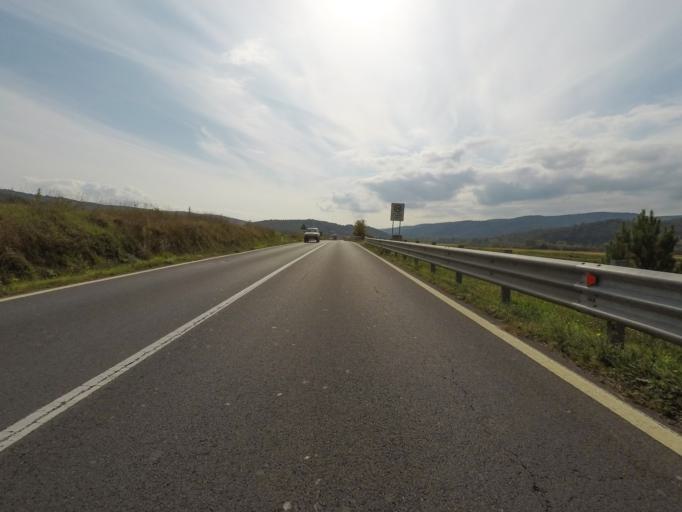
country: IT
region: Tuscany
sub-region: Provincia di Siena
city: Murlo
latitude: 43.1652
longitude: 11.2873
